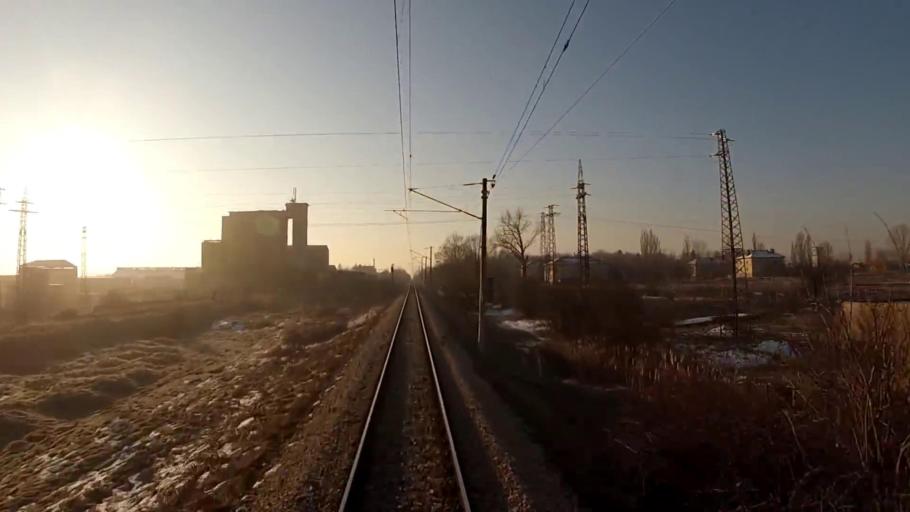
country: BG
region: Sofiya
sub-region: Obshtina Kostinbrod
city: Kostinbrod
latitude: 42.7911
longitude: 23.2104
